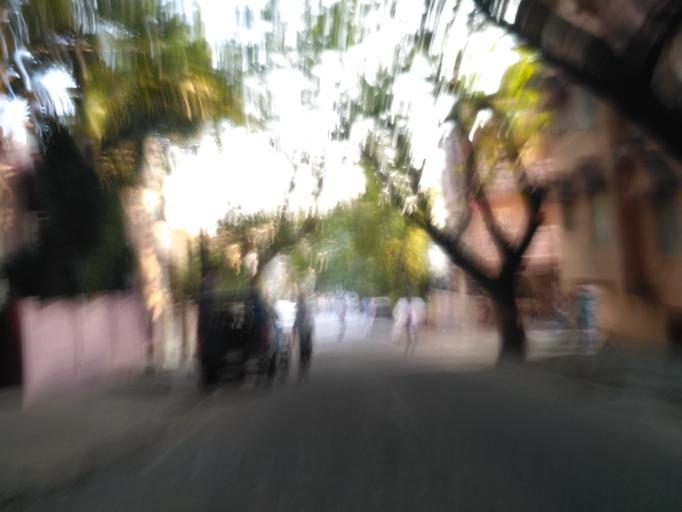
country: IN
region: Karnataka
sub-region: Bangalore Urban
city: Bangalore
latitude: 12.9662
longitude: 77.5384
